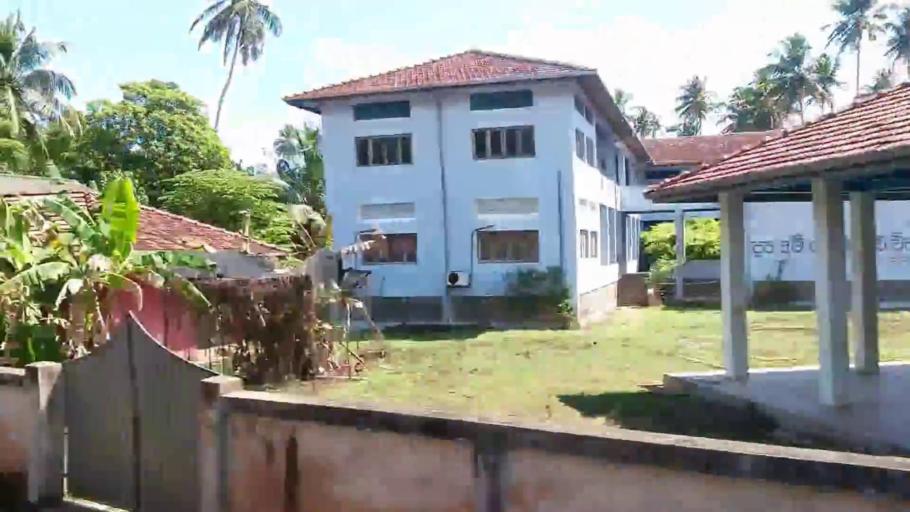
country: LK
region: Southern
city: Hikkaduwa
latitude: 6.1638
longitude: 80.0920
